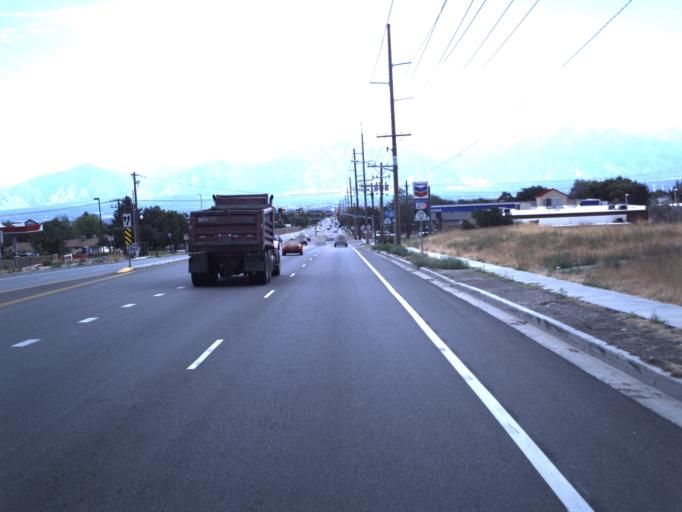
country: US
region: Utah
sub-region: Salt Lake County
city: Oquirrh
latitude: 40.6530
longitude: -112.0269
